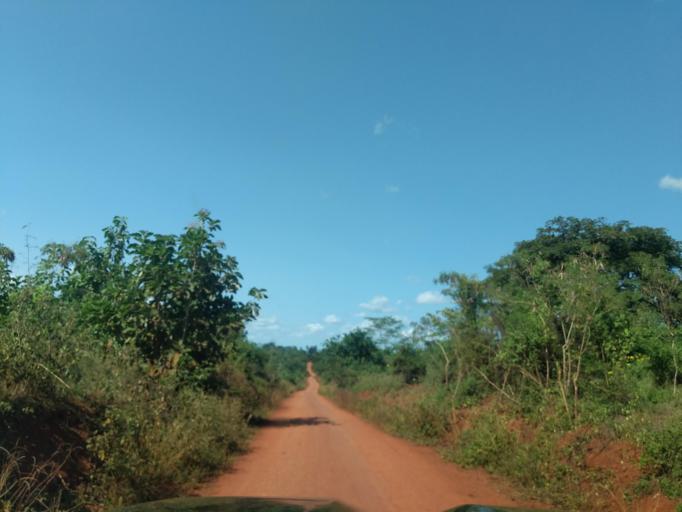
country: TZ
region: Tanga
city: Muheza
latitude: -5.3758
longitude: 38.5809
